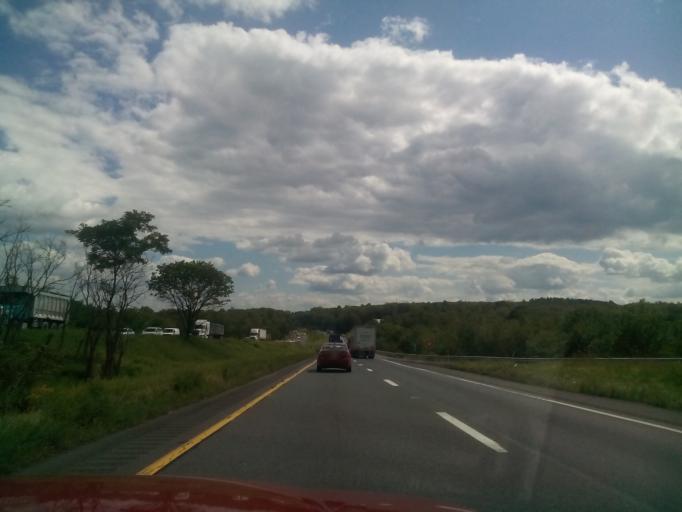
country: US
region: Pennsylvania
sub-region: Monroe County
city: Tannersville
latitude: 41.0368
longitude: -75.3119
